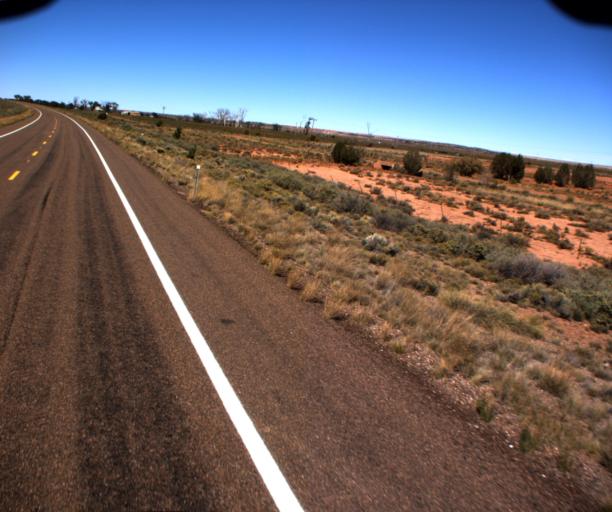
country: US
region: Arizona
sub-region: Apache County
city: Saint Johns
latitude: 34.6115
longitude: -109.6507
